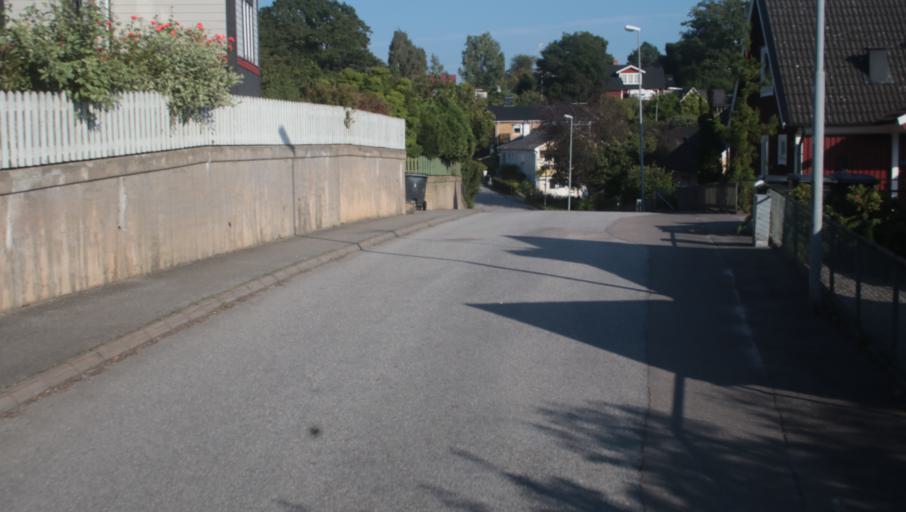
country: SE
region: Blekinge
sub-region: Karlshamns Kommun
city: Karlshamn
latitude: 56.1829
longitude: 14.8574
